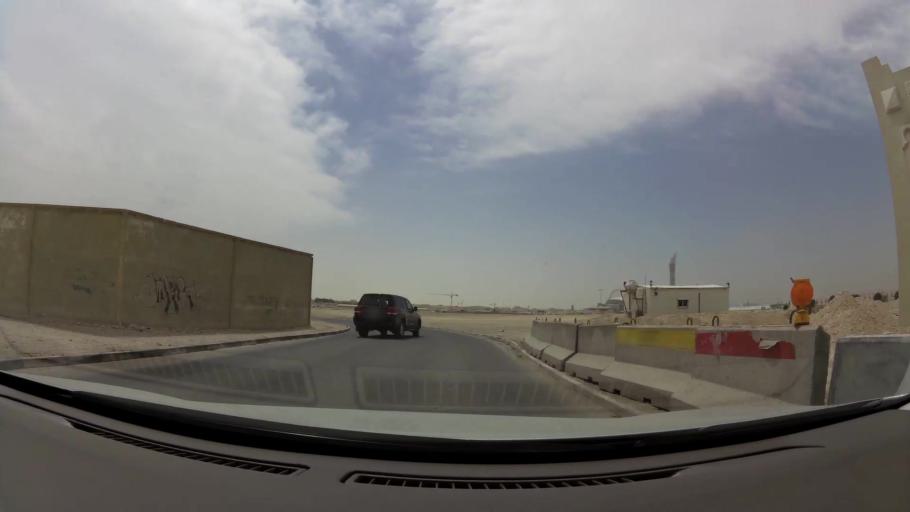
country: QA
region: Baladiyat ar Rayyan
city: Ar Rayyan
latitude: 25.2778
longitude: 51.4606
